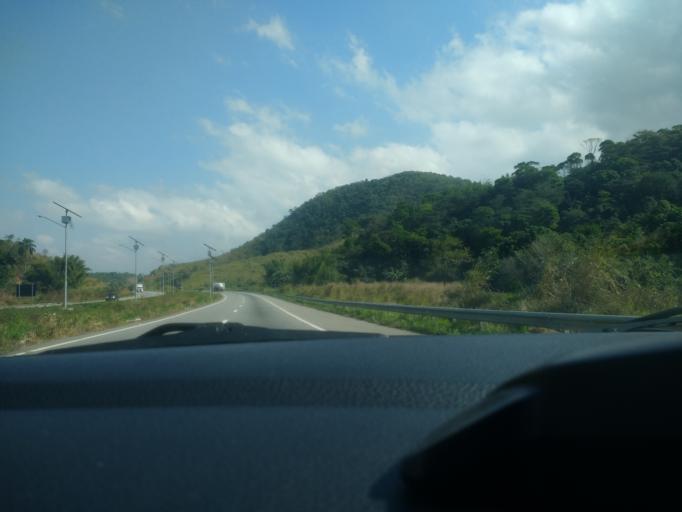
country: BR
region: Rio de Janeiro
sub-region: Queimados
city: Queimados
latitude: -22.6873
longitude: -43.4875
